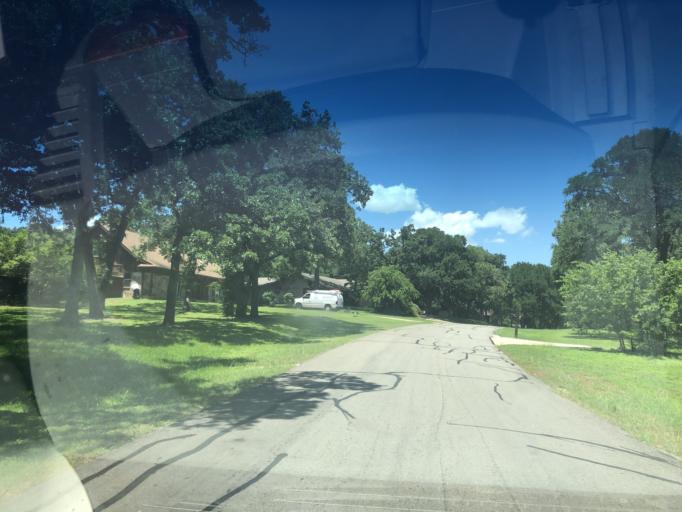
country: US
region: Texas
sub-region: Dallas County
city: Grand Prairie
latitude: 32.7765
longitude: -97.0316
